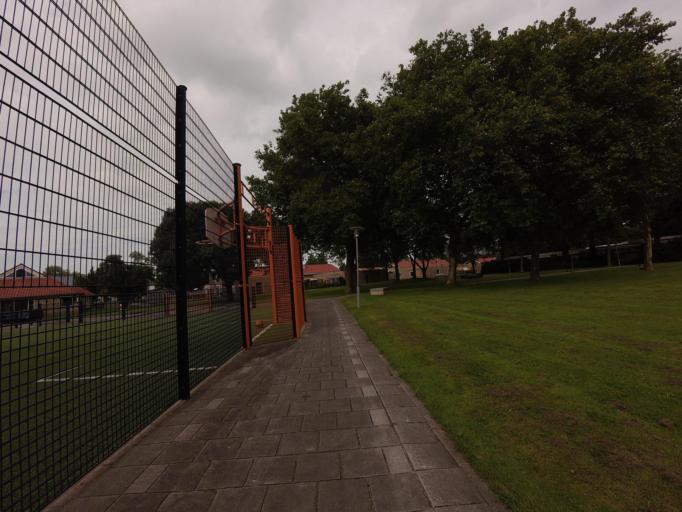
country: NL
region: South Holland
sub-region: Bodegraven-Reeuwijk
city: Bodegraven
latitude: 52.1066
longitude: 4.7154
